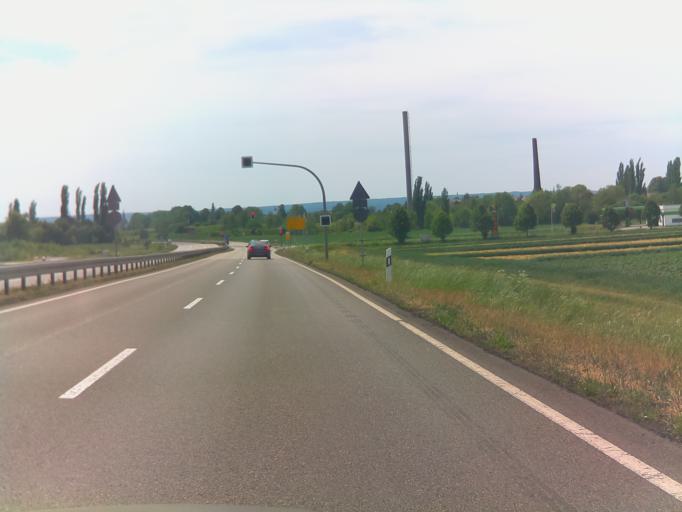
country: DE
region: Saxony-Anhalt
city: Egeln
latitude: 51.9636
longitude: 11.4498
